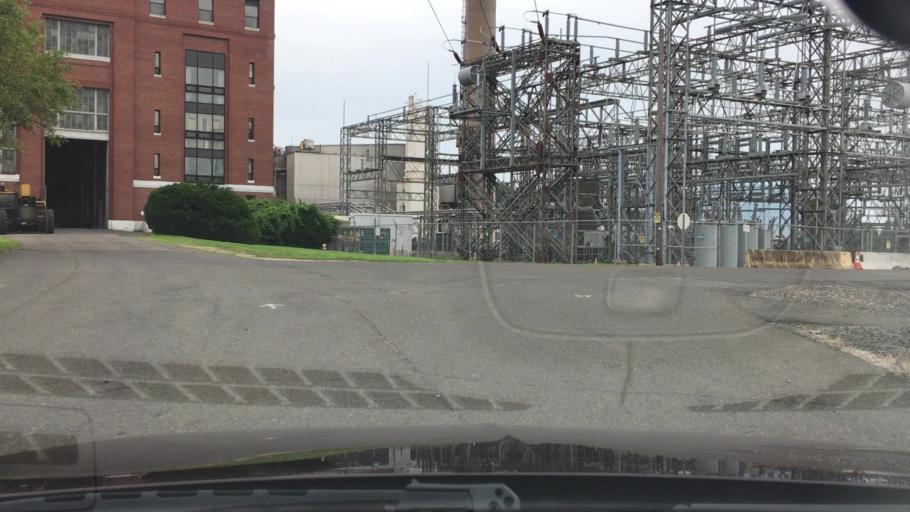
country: US
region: Connecticut
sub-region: Hartford County
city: Hartford
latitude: 41.7505
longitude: -72.6536
